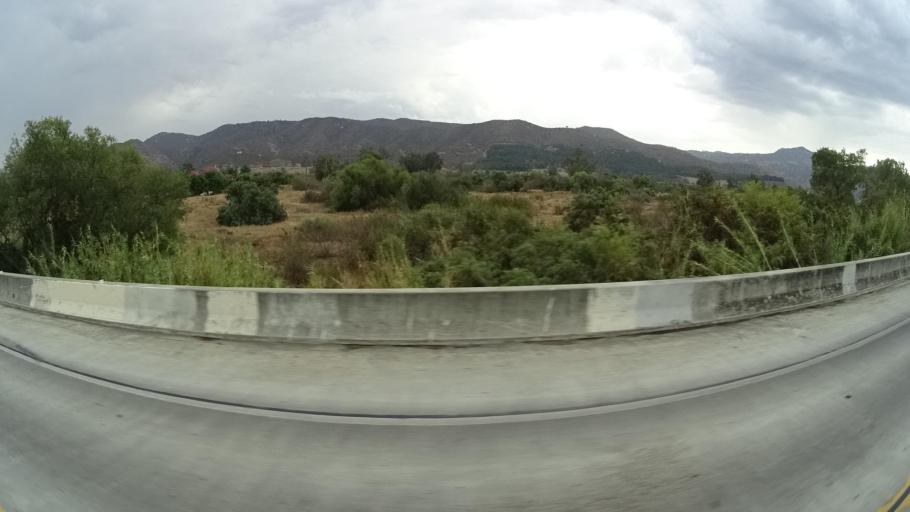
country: US
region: California
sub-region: San Diego County
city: San Pasqual
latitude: 33.0947
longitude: -116.9614
